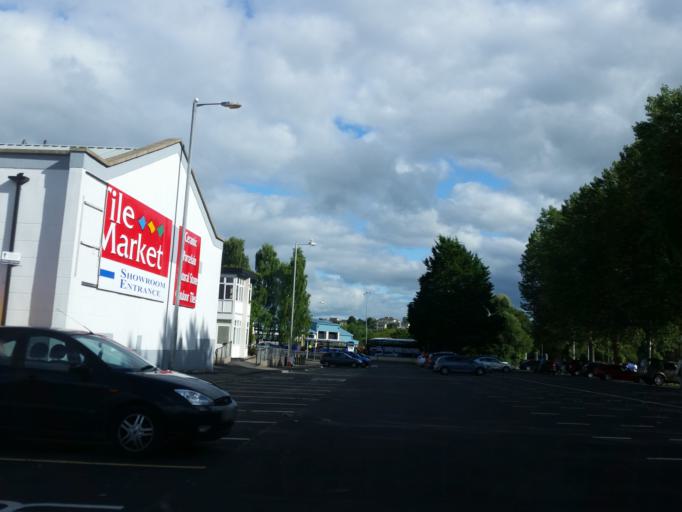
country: GB
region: Northern Ireland
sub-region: Fermanagh District
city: Enniskillen
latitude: 54.3445
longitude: -7.6416
